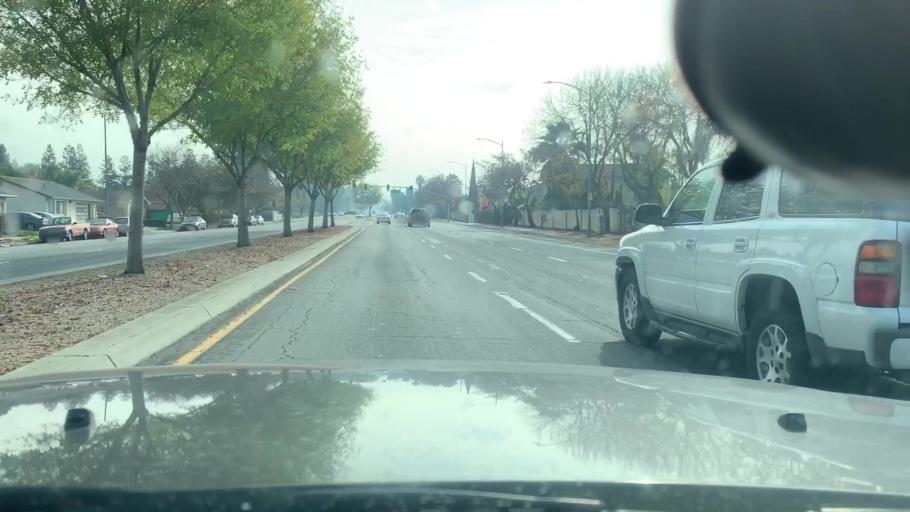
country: US
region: California
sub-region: Santa Clara County
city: Alum Rock
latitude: 37.3317
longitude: -121.7994
